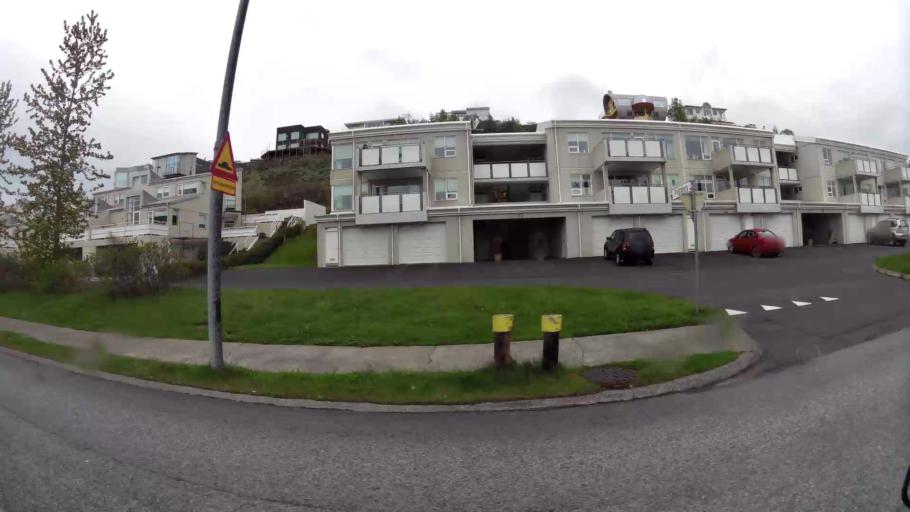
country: IS
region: Capital Region
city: Hafnarfjoerdur
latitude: 64.0639
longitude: -21.9270
